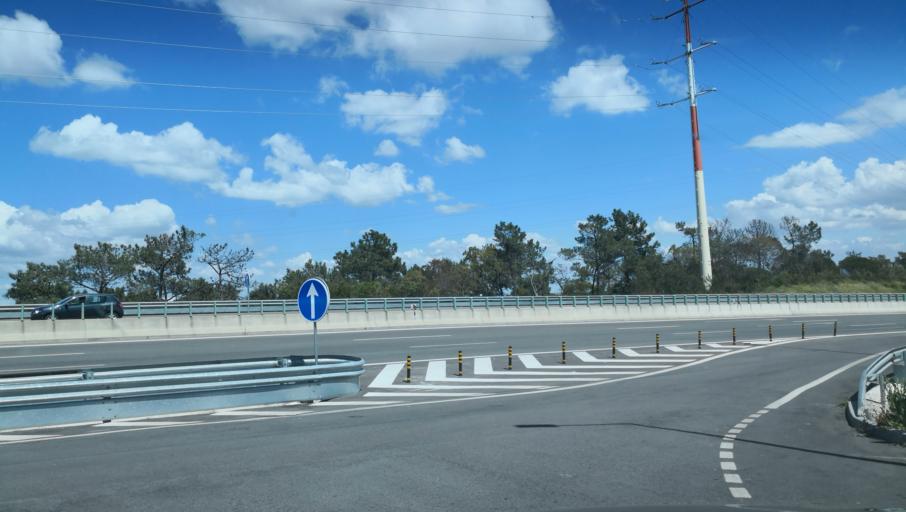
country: PT
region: Setubal
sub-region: Almada
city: Sobreda
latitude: 38.6378
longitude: -9.1986
